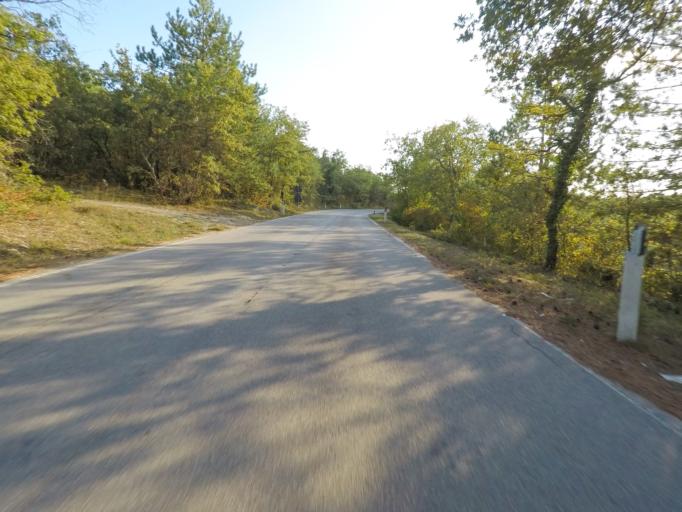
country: IT
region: Tuscany
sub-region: Provincia di Siena
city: Radda in Chianti
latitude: 43.4556
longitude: 11.3838
